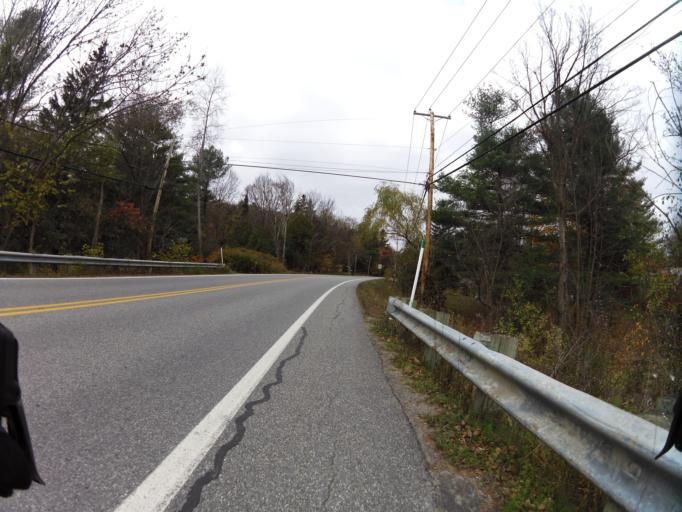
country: CA
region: Quebec
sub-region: Outaouais
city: Gatineau
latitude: 45.5274
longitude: -75.8046
